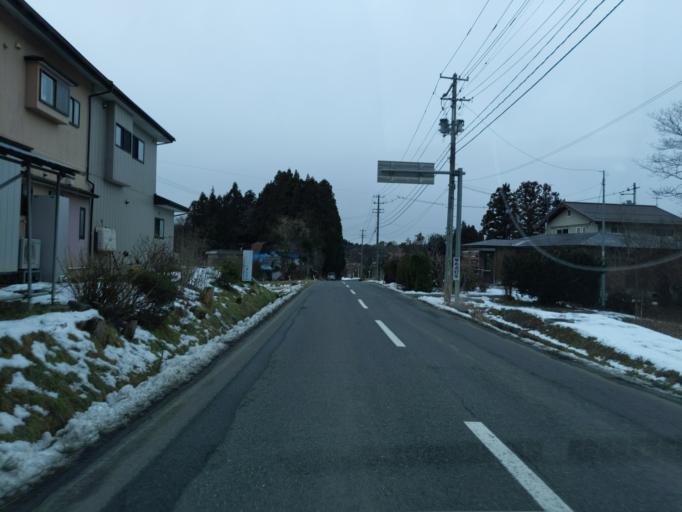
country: JP
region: Iwate
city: Mizusawa
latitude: 39.1794
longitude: 141.2675
